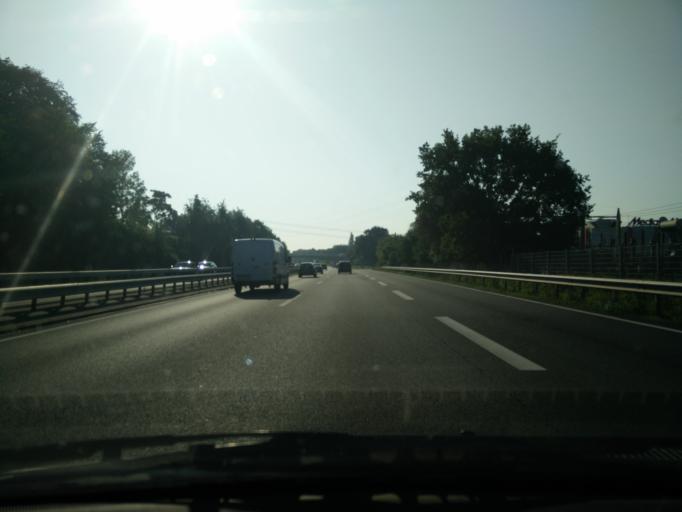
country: DE
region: Schleswig-Holstein
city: Halstenbek
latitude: 53.6303
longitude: 9.8661
